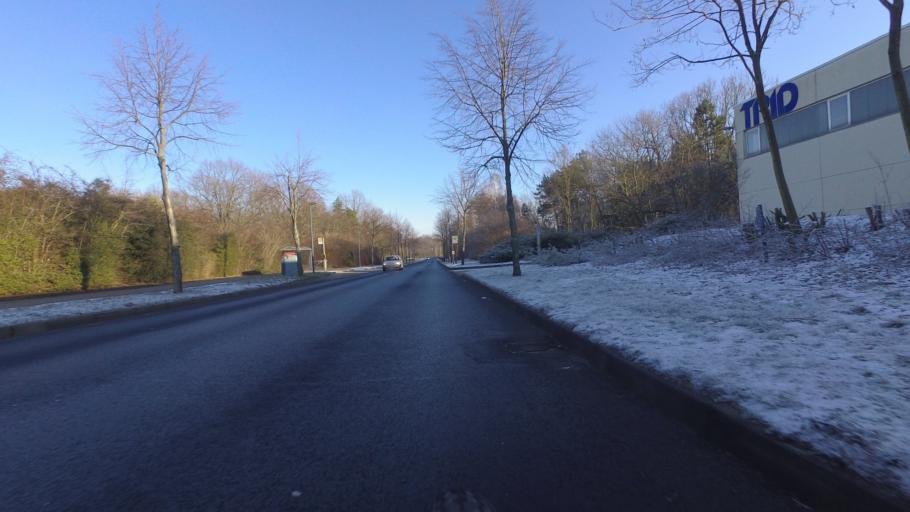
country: DE
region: Brandenburg
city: Ludwigsfelde
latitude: 52.3110
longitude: 13.2939
